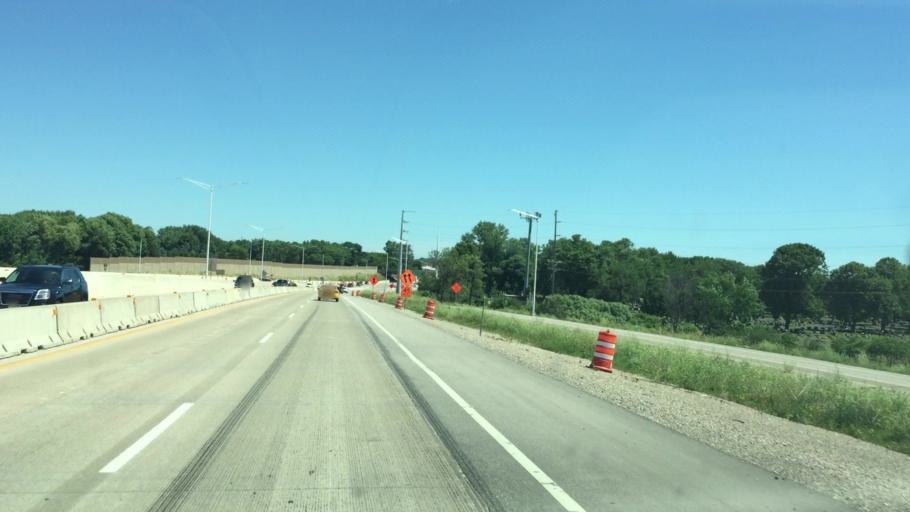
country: US
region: Wisconsin
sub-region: Winnebago County
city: Menasha
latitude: 44.2210
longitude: -88.4484
